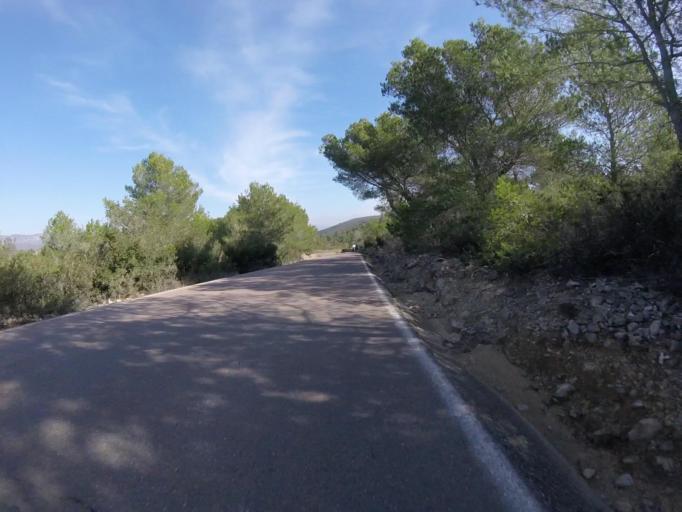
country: ES
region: Valencia
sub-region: Provincia de Castello
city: Benlloch
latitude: 40.2445
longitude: 0.0784
